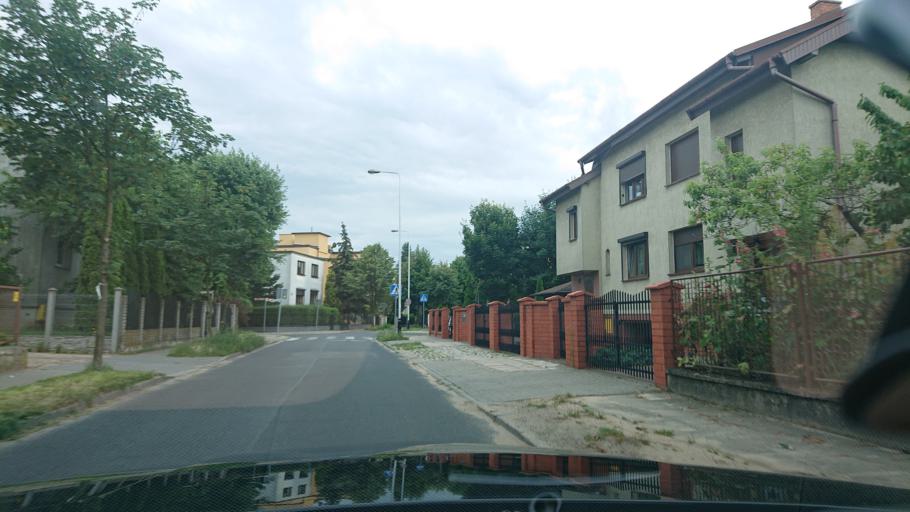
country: PL
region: Greater Poland Voivodeship
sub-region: Powiat gnieznienski
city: Gniezno
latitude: 52.5365
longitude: 17.6157
